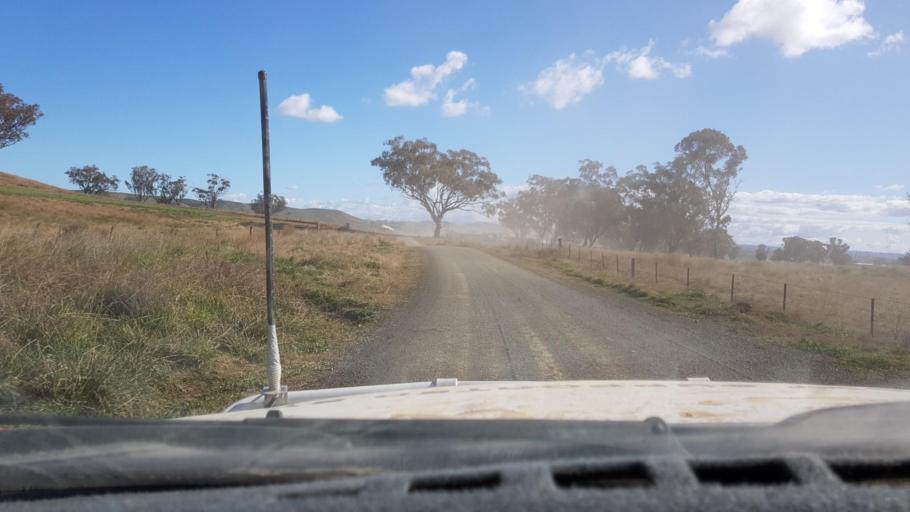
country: AU
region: New South Wales
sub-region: Narrabri
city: Blair Athol
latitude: -30.5384
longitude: 150.4501
